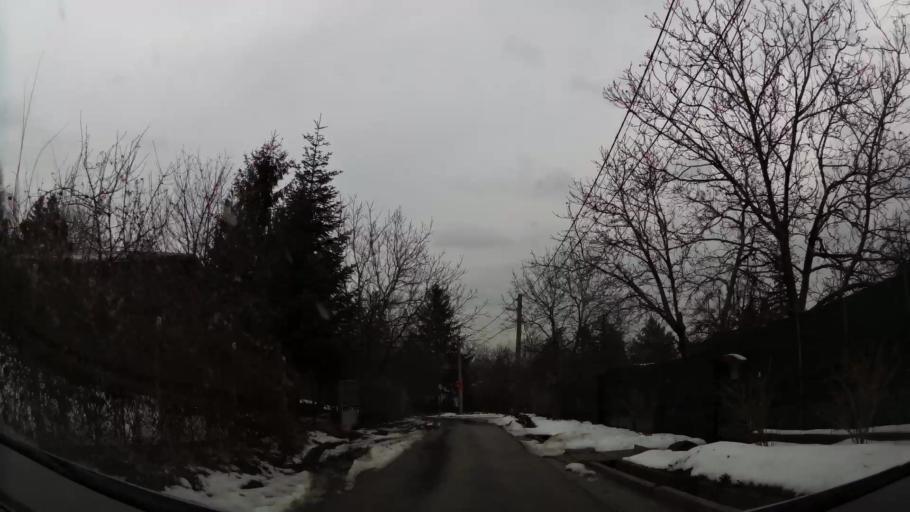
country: BG
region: Sofiya
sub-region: Obshtina Bozhurishte
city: Bozhurishte
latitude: 42.6726
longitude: 23.2284
